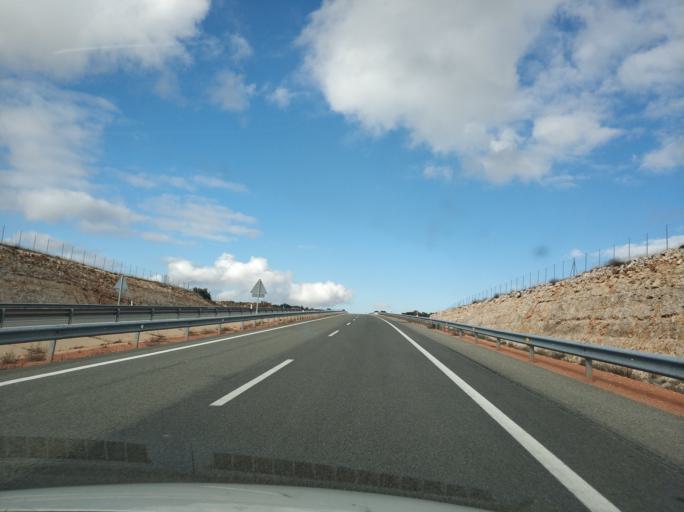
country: ES
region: Castille and Leon
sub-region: Provincia de Soria
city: Adradas
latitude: 41.2958
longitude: -2.4770
